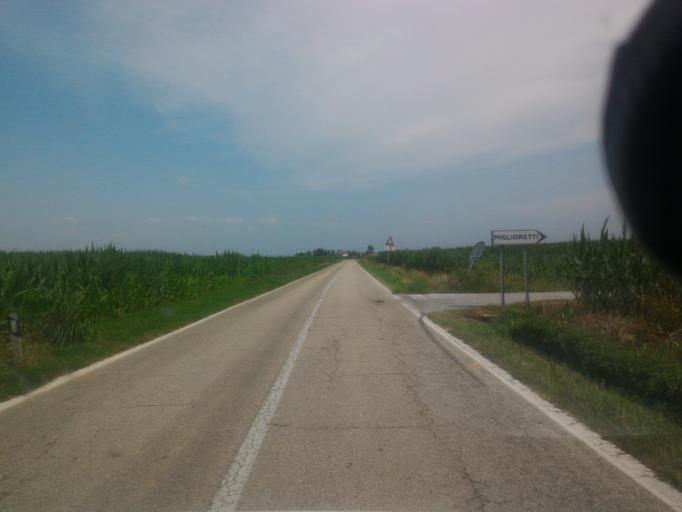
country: IT
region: Piedmont
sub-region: Provincia di Torino
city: Buriasco
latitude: 44.8598
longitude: 7.4274
